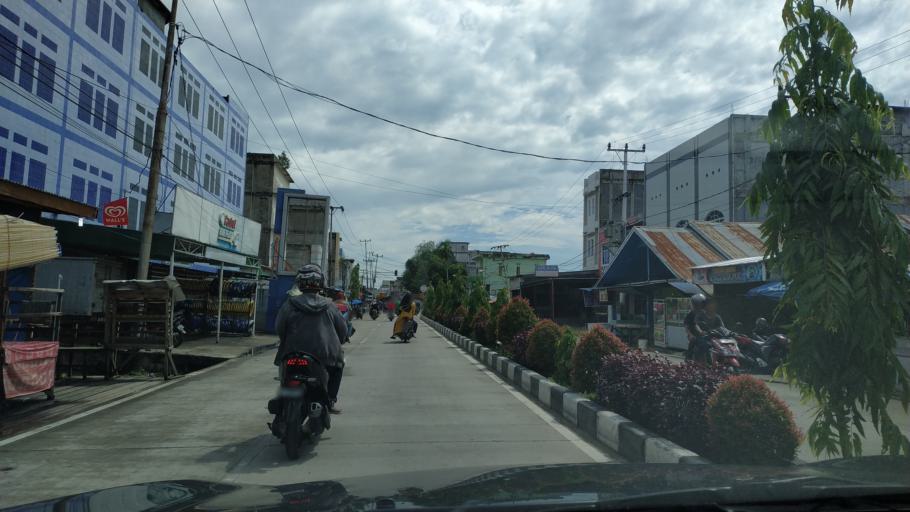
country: ID
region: Riau
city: Tembilahan
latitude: -0.3247
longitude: 103.1480
